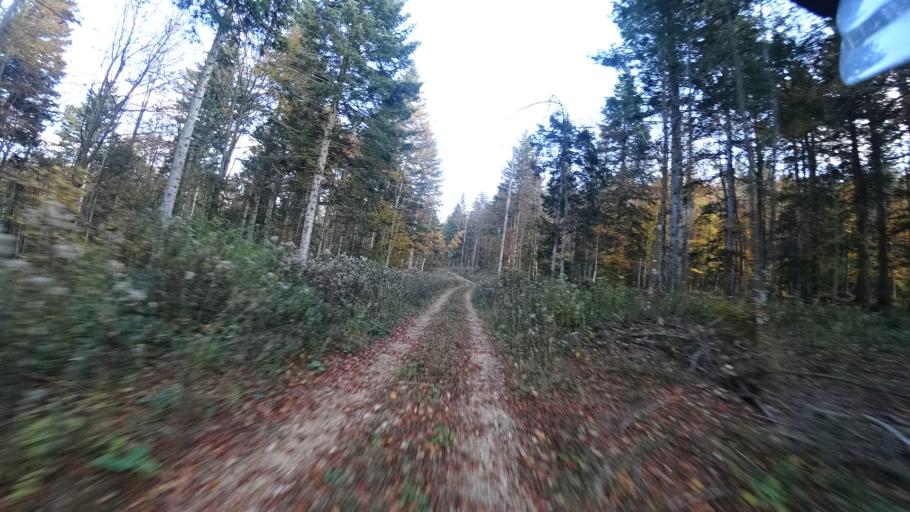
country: HR
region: Karlovacka
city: Plaski
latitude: 44.9670
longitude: 15.3870
